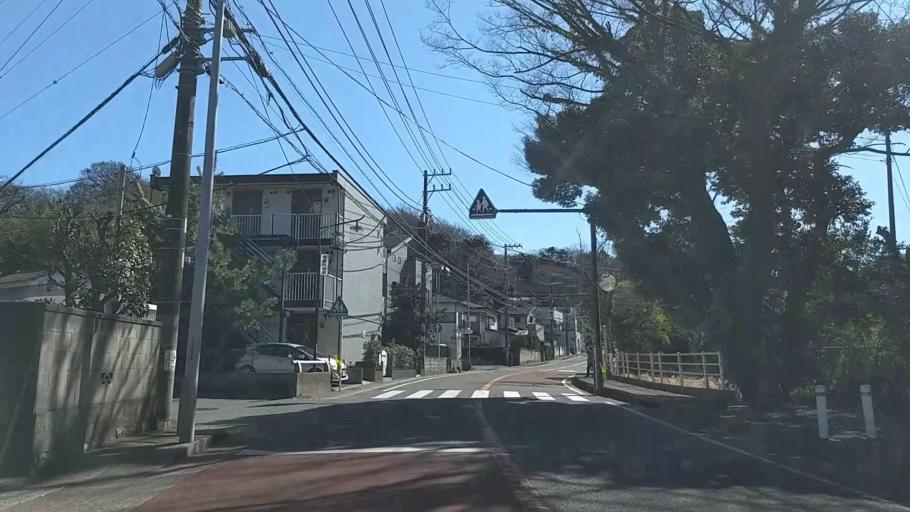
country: JP
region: Kanagawa
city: Kamakura
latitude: 35.3214
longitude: 139.5275
